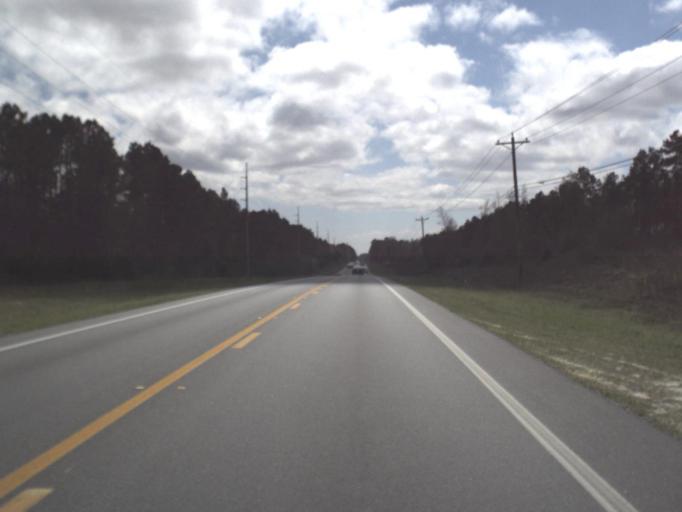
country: US
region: Florida
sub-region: Wakulla County
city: Crawfordville
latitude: 30.2591
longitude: -84.3622
